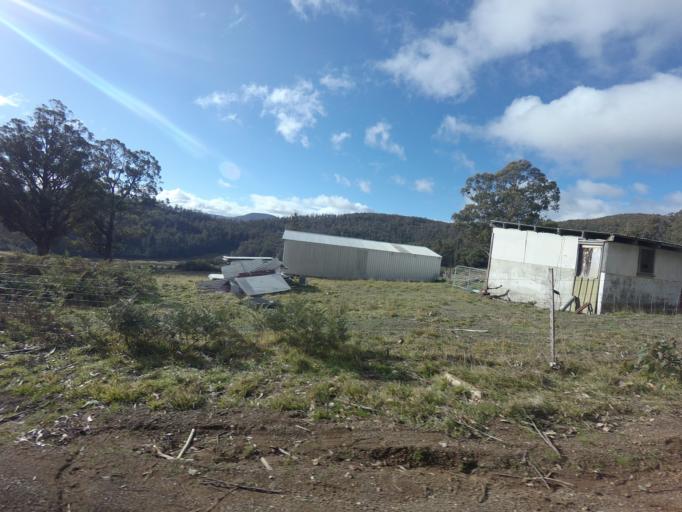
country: AU
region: Tasmania
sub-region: Derwent Valley
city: New Norfolk
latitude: -42.8404
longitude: 147.1362
